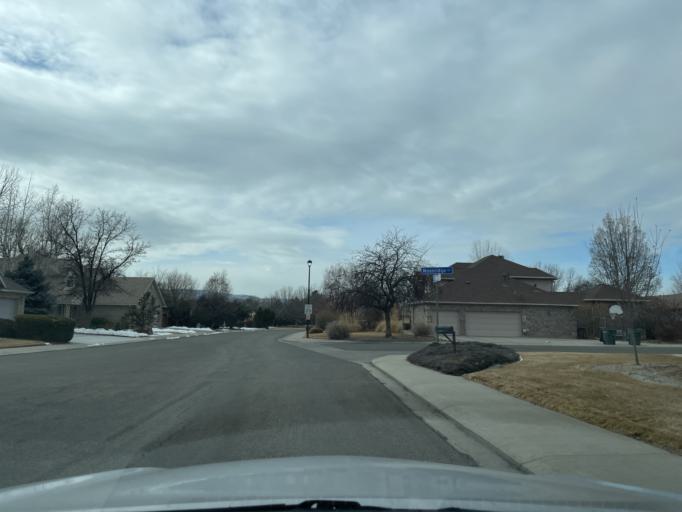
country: US
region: Colorado
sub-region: Mesa County
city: Grand Junction
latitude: 39.1038
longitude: -108.5805
